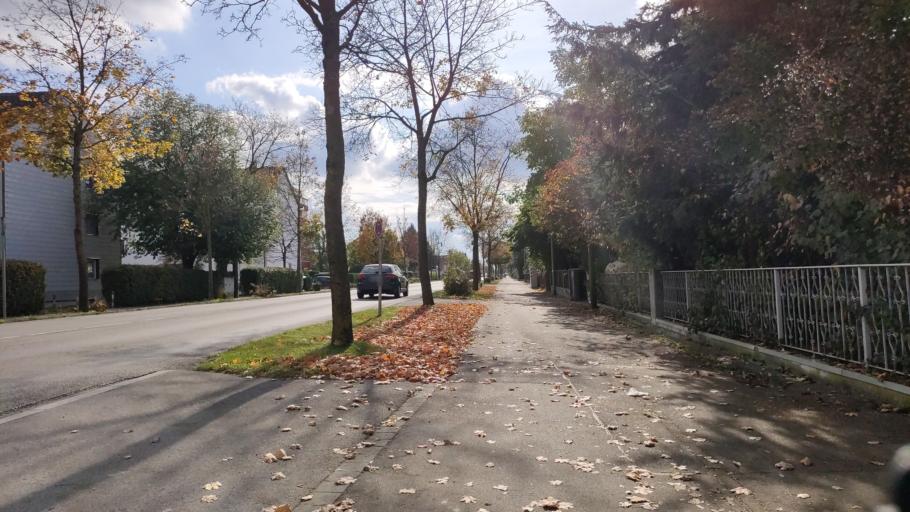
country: DE
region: Bavaria
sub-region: Swabia
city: Konigsbrunn
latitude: 48.2625
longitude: 10.8847
